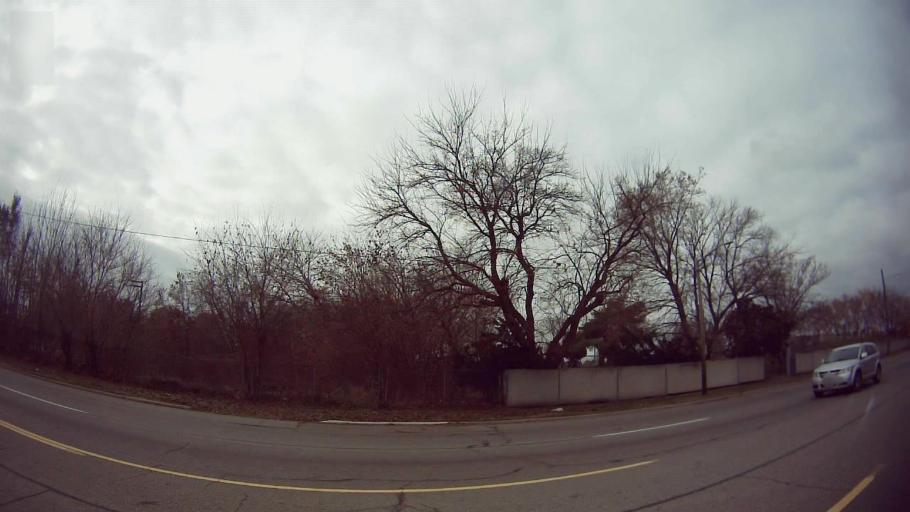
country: US
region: Michigan
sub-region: Wayne County
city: Hamtramck
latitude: 42.3998
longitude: -83.0229
